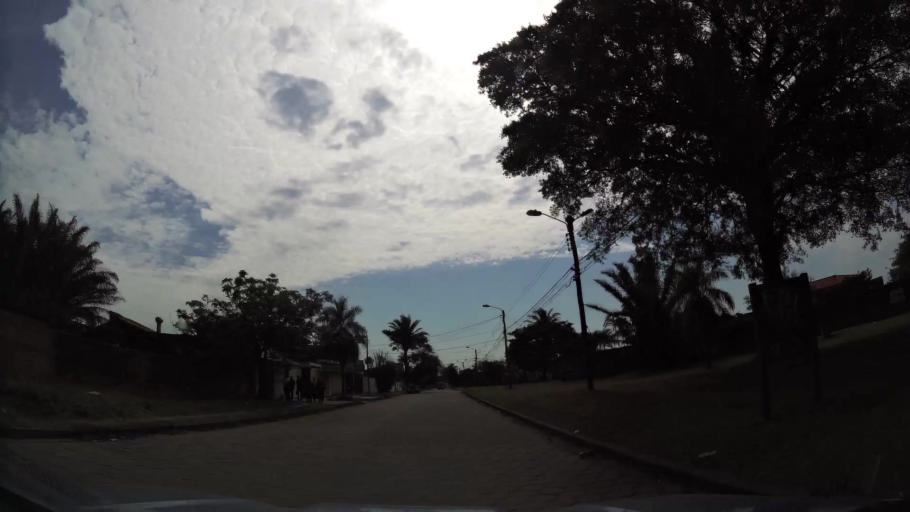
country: BO
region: Santa Cruz
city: Santa Cruz de la Sierra
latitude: -17.7486
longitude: -63.1563
